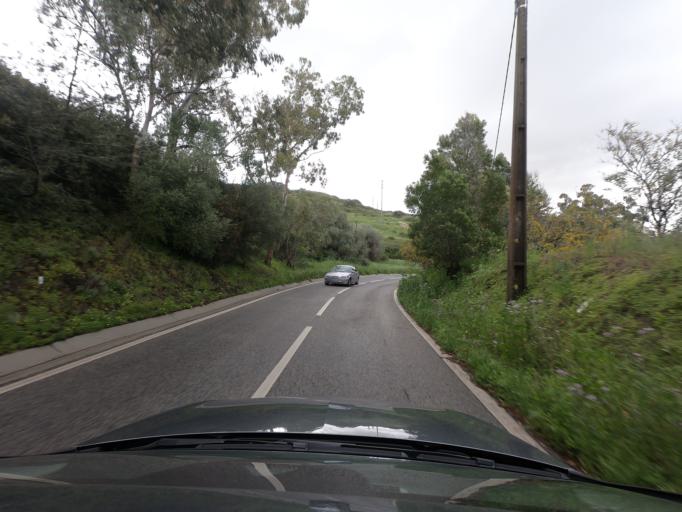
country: PT
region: Lisbon
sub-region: Oeiras
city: Quejas
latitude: 38.7395
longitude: -9.2618
